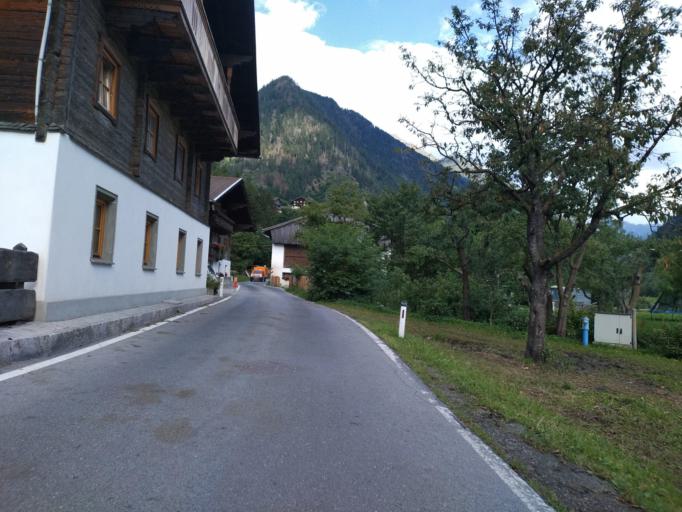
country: AT
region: Tyrol
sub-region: Politischer Bezirk Lienz
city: Hopfgarten in Defereggen
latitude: 46.9253
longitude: 12.5857
